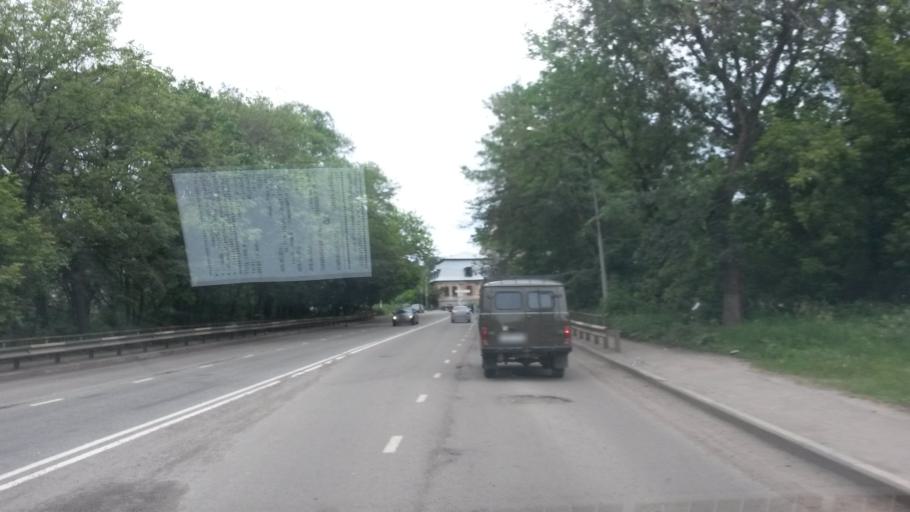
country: RU
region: Jaroslavl
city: Yaroslavl
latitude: 57.6080
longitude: 39.8410
